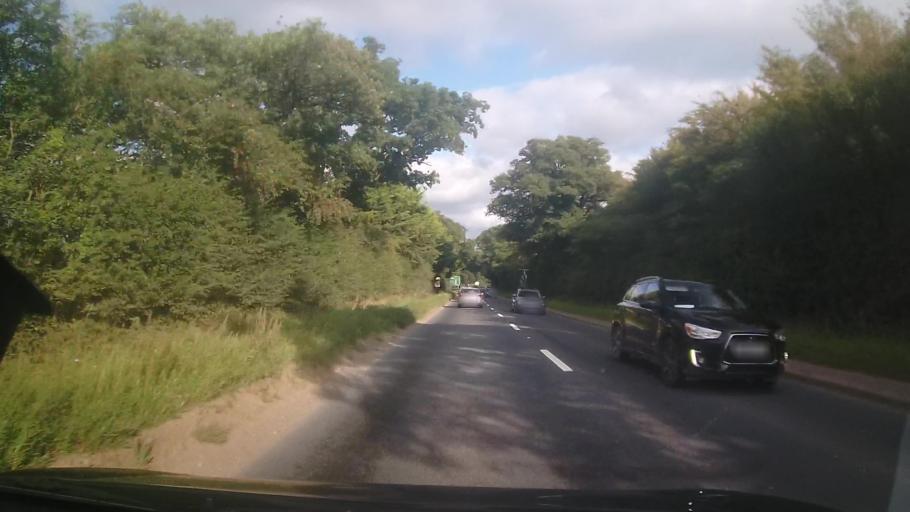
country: GB
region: England
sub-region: Shropshire
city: Bromfield
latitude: 52.3890
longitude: -2.7481
